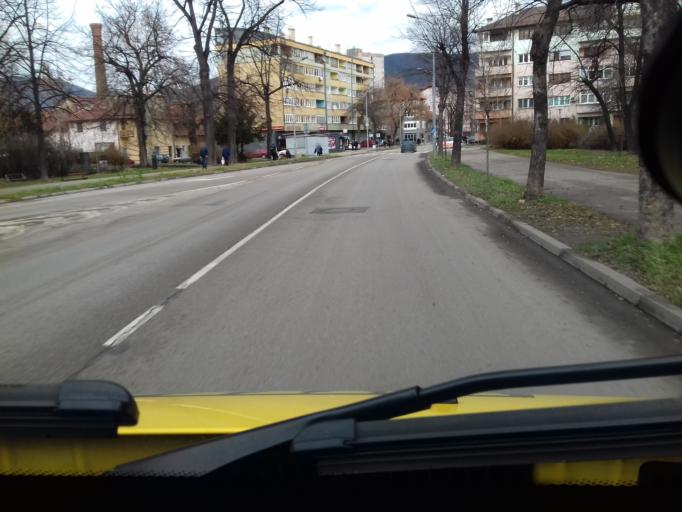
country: BA
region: Federation of Bosnia and Herzegovina
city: Zenica
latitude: 44.2080
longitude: 17.9081
